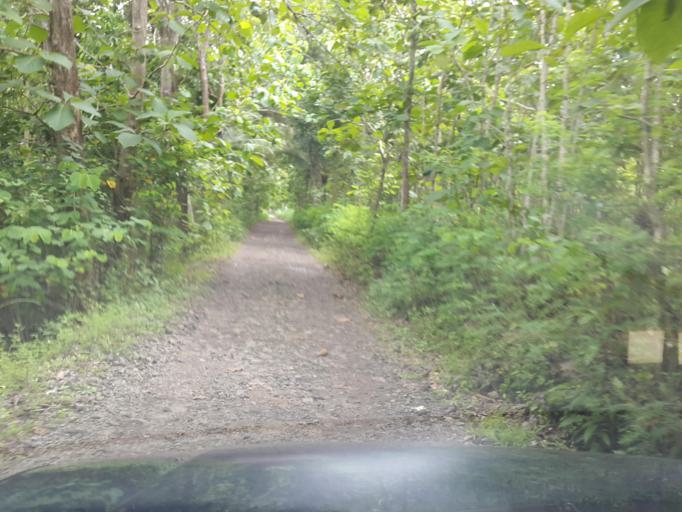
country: ID
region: Daerah Istimewa Yogyakarta
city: Wonosari
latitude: -7.9229
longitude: 110.6397
